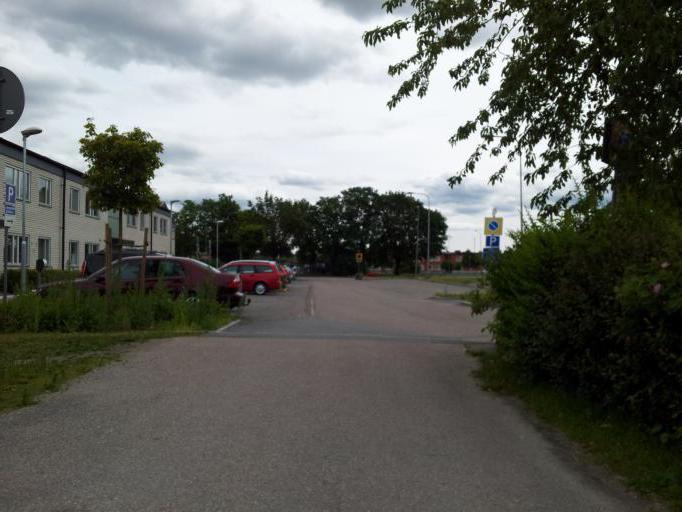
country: SE
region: Uppsala
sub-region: Uppsala Kommun
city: Uppsala
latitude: 59.8715
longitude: 17.6460
